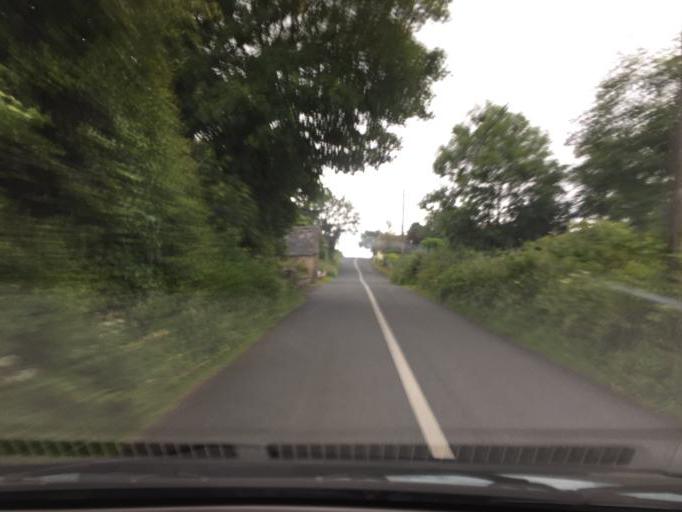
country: IE
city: Ballisodare
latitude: 54.2587
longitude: -8.5341
